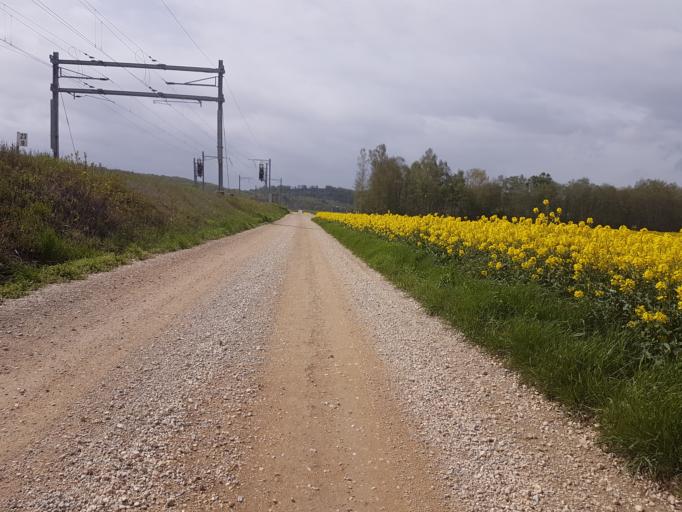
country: CH
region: Vaud
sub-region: Jura-Nord vaudois District
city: Bavois
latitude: 46.6784
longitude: 6.5557
